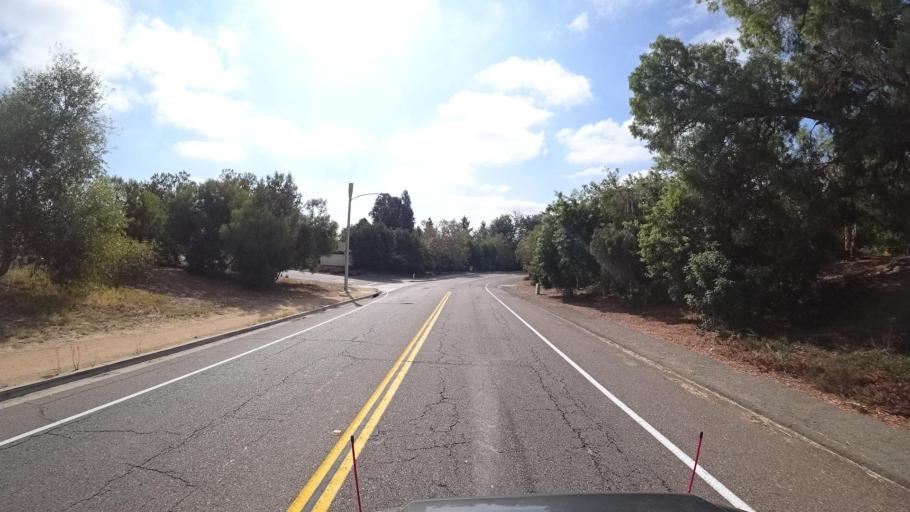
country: US
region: California
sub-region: San Diego County
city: Rancho Santa Fe
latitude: 33.0545
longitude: -117.2329
